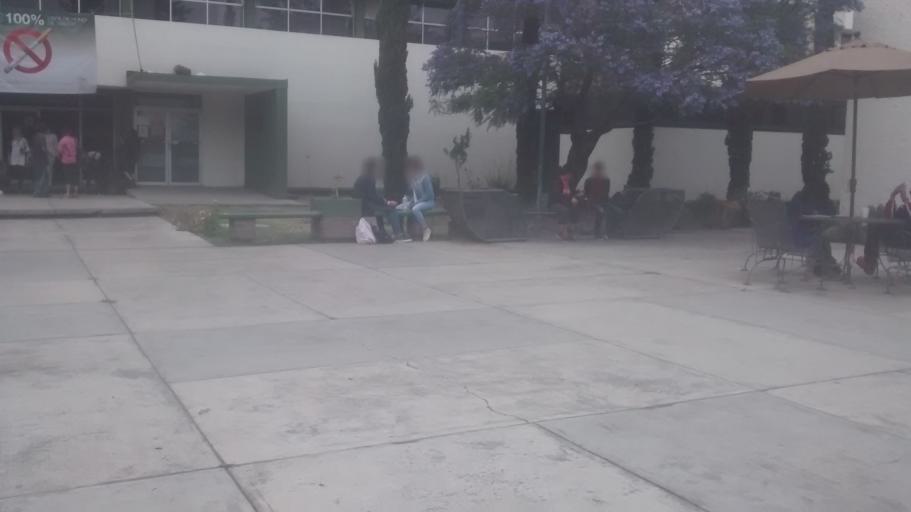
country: MX
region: Mexico
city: San Buenaventura
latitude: 19.2798
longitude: -99.6777
